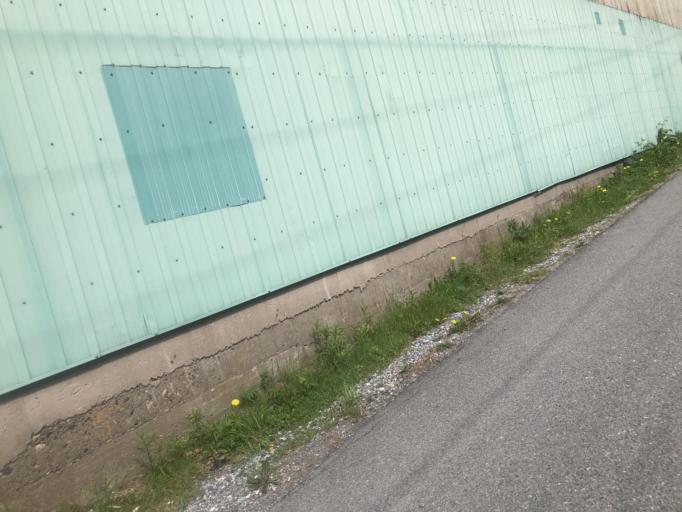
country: CA
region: New Brunswick
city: Saint John
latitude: 45.2741
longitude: -66.0880
